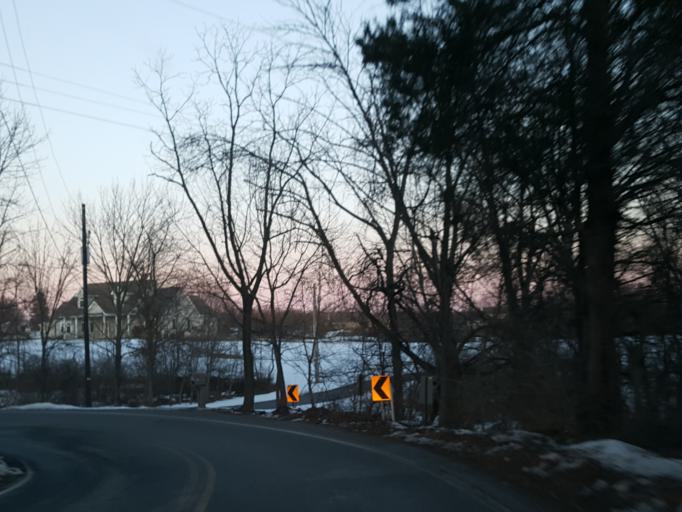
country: US
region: Pennsylvania
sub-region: Dauphin County
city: Hummelstown
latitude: 40.2836
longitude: -76.7285
